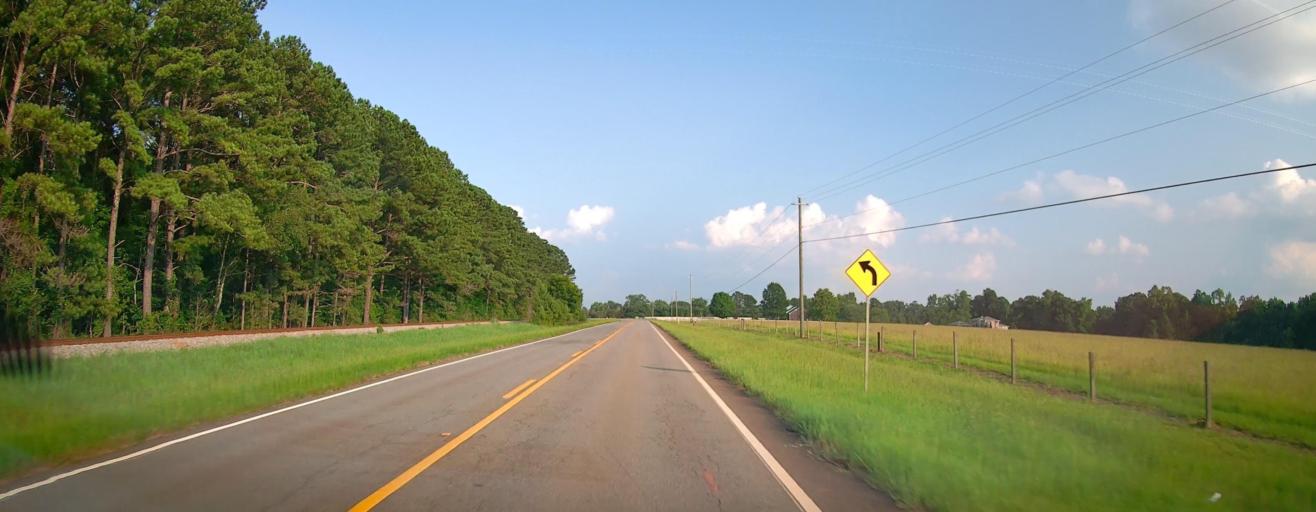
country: US
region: Georgia
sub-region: Jones County
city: Gray
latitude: 33.0447
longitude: -83.5529
